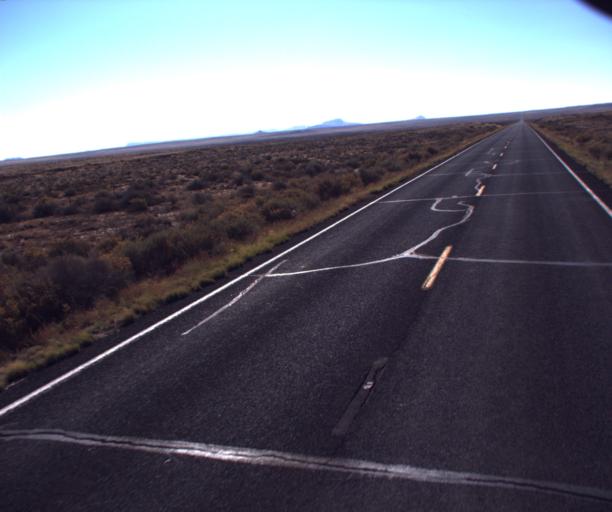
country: US
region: Arizona
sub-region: Navajo County
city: First Mesa
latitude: 35.7025
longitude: -110.5083
